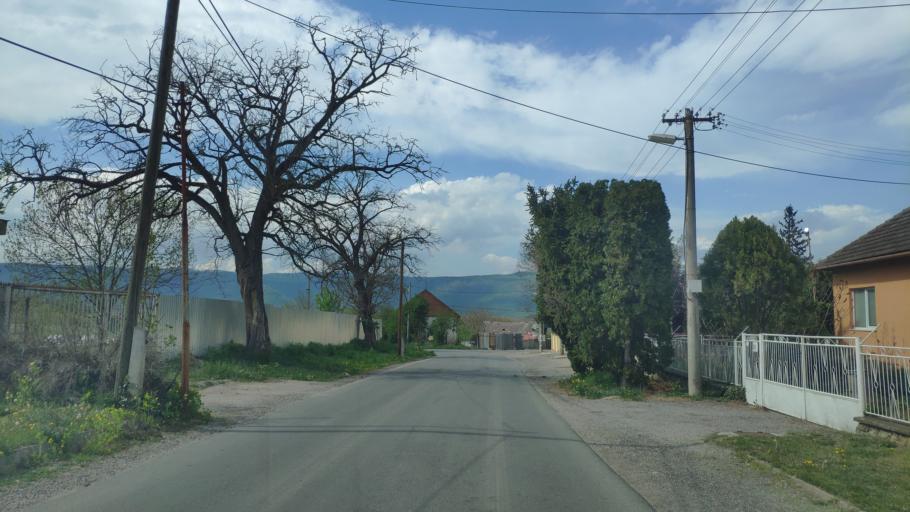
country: SK
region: Kosicky
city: Moldava nad Bodvou
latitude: 48.5845
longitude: 20.9208
